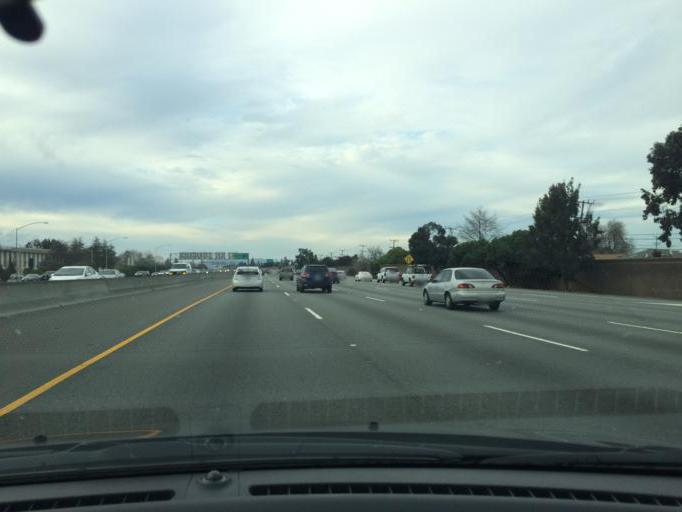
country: US
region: California
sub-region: San Mateo County
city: San Mateo
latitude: 37.5571
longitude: -122.2996
